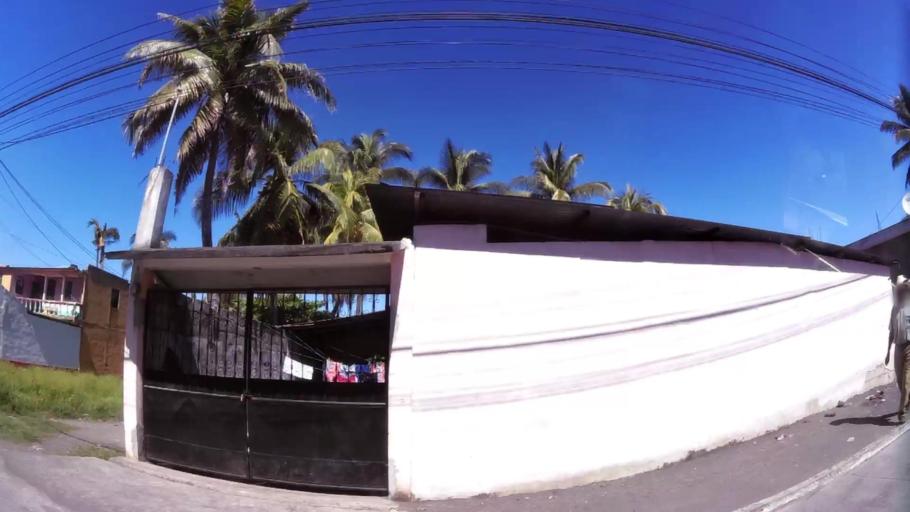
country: GT
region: Escuintla
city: Iztapa
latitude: 13.9306
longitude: -90.7123
